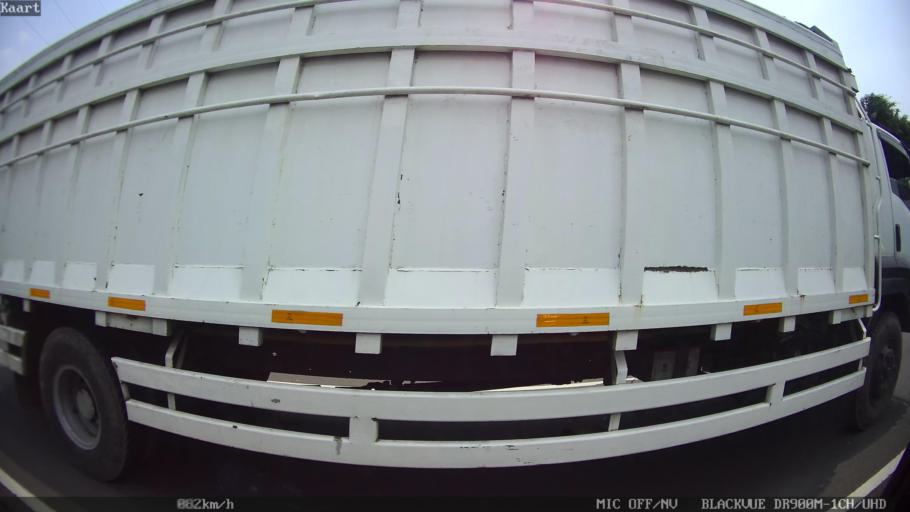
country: ID
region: Banten
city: Curug
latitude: -5.9843
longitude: 106.0333
